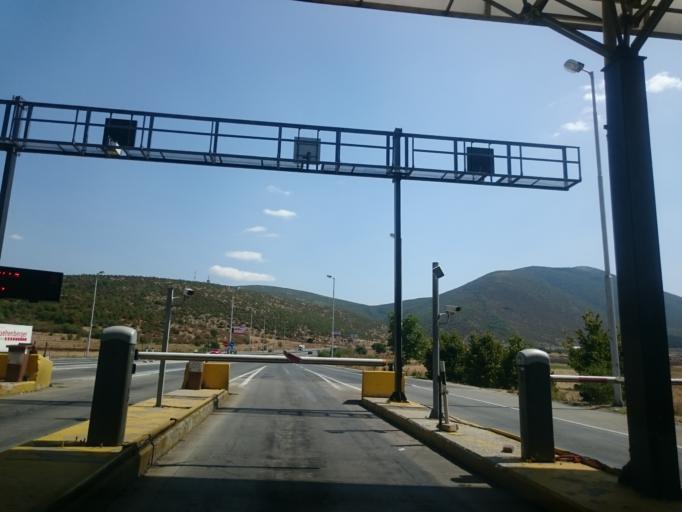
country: MK
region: Zelino
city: Zhelino
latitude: 41.9898
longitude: 21.0770
